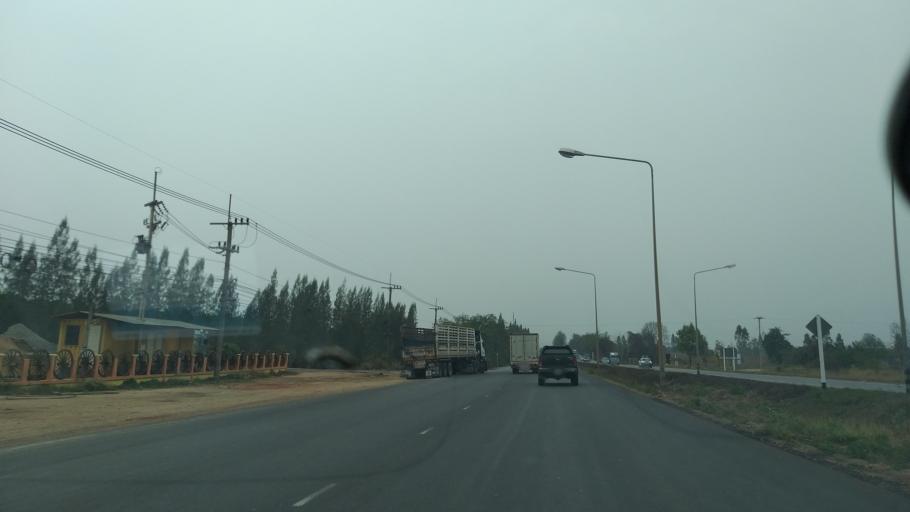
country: TH
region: Chachoengsao
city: Plaeng Yao
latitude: 13.5133
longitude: 101.2678
